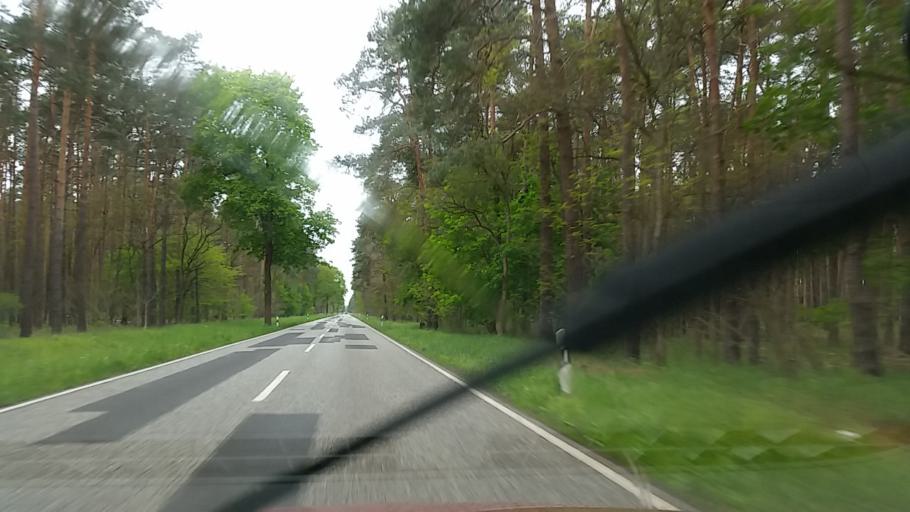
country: DE
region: Brandenburg
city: Spreenhagen
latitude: 52.3251
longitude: 13.9359
